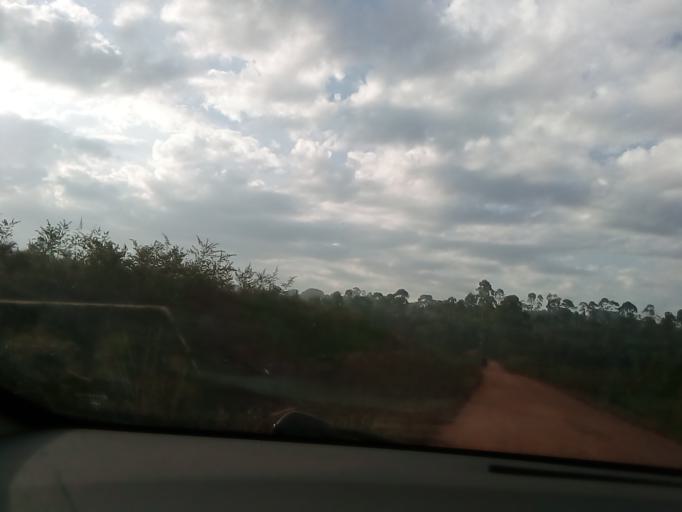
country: UG
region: Central Region
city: Masaka
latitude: -0.3465
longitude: 31.7092
